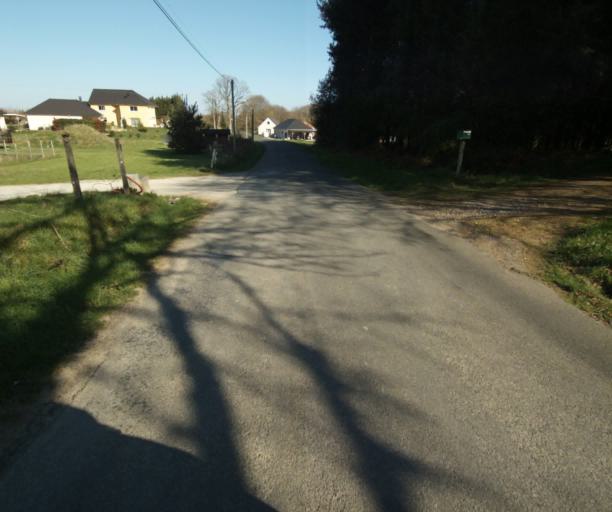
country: FR
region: Limousin
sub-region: Departement de la Correze
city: Saint-Mexant
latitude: 45.2957
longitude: 1.6920
